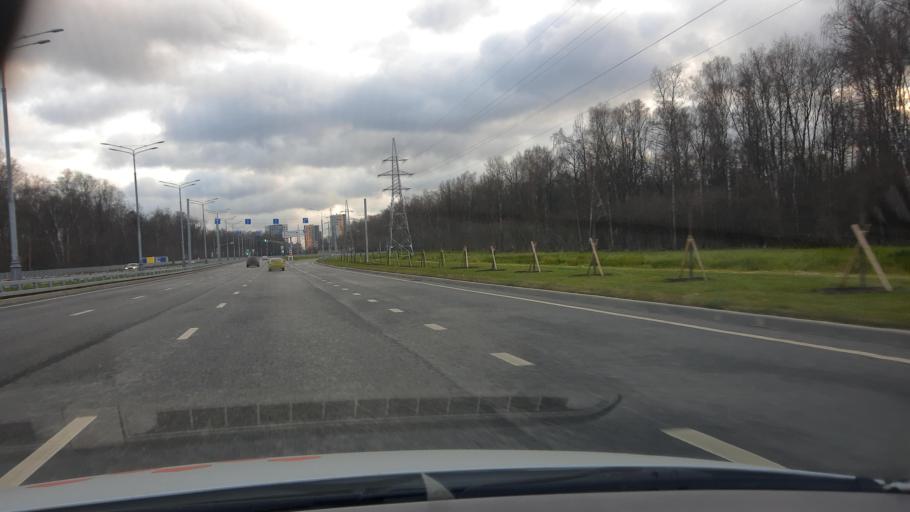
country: RU
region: Moskovskaya
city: Kommunarka
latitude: 55.5900
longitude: 37.4813
